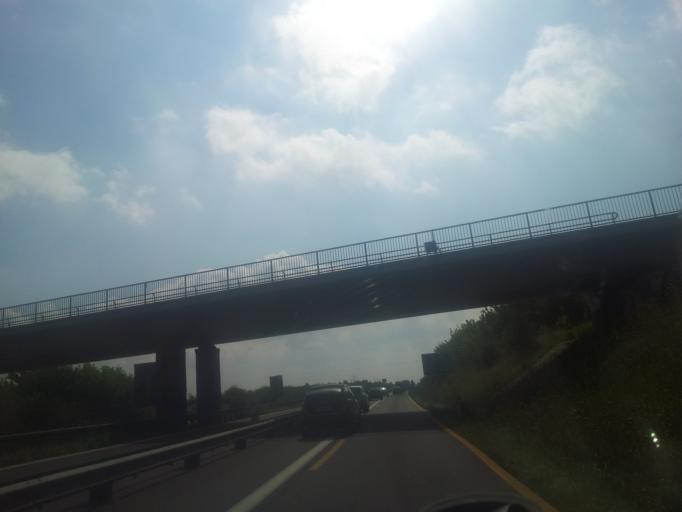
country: DE
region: Saxony-Anhalt
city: Konnern
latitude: 51.6794
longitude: 11.7817
